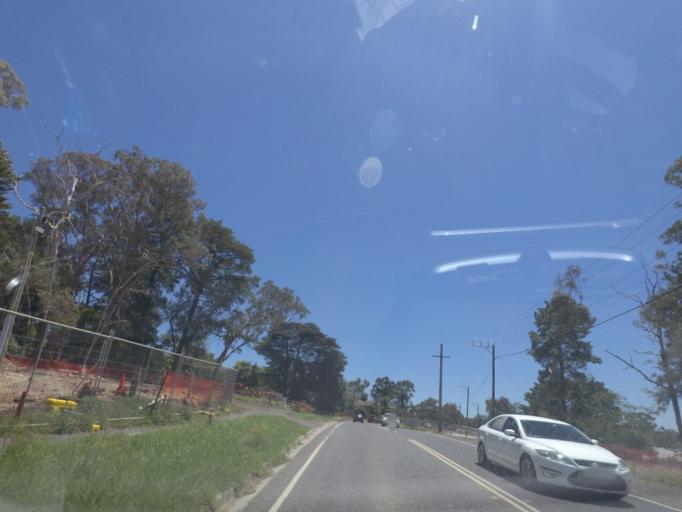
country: AU
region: Victoria
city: Plenty
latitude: -37.6646
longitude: 145.1238
